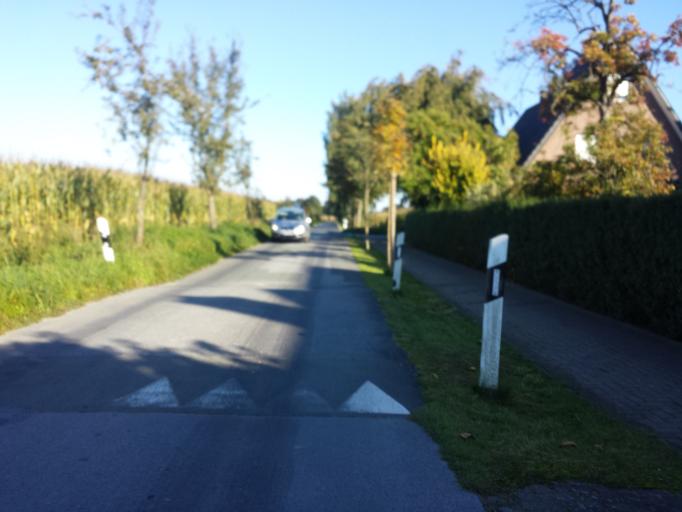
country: DE
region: North Rhine-Westphalia
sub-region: Regierungsbezirk Detmold
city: Langenberg
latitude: 51.7667
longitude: 8.3314
